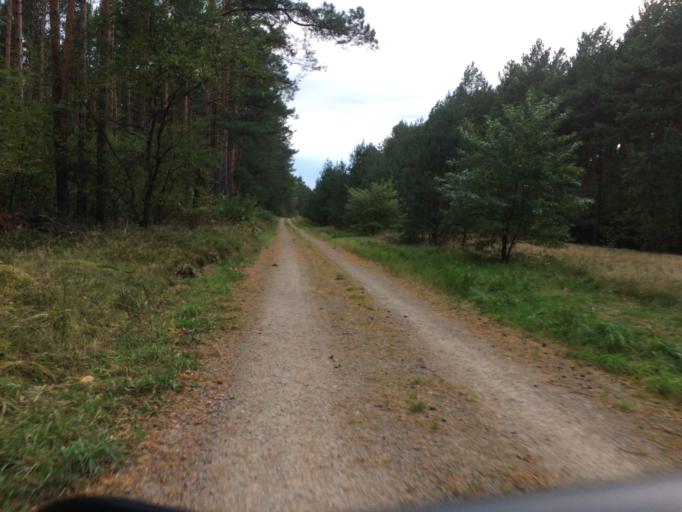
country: DE
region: Brandenburg
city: Birkenwerder
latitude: 52.7039
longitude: 13.3239
